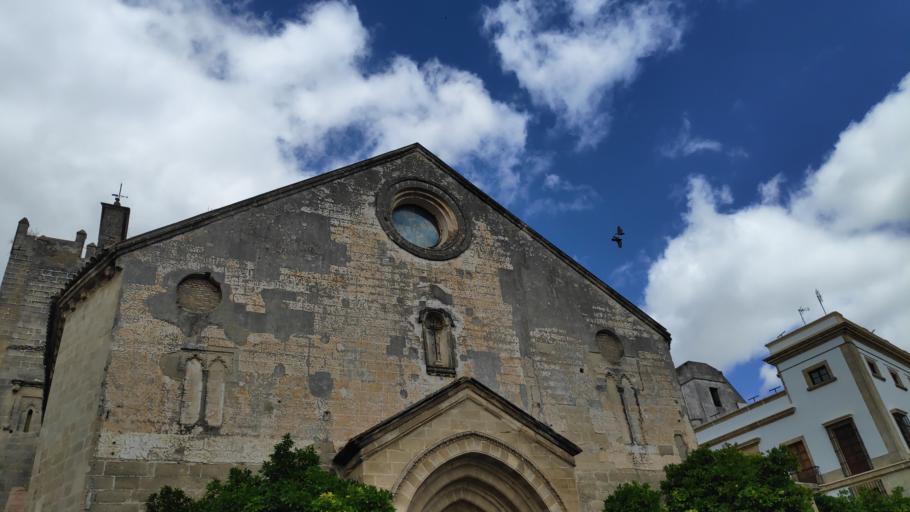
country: ES
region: Andalusia
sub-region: Provincia de Cadiz
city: Jerez de la Frontera
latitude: 36.6835
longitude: -6.1388
